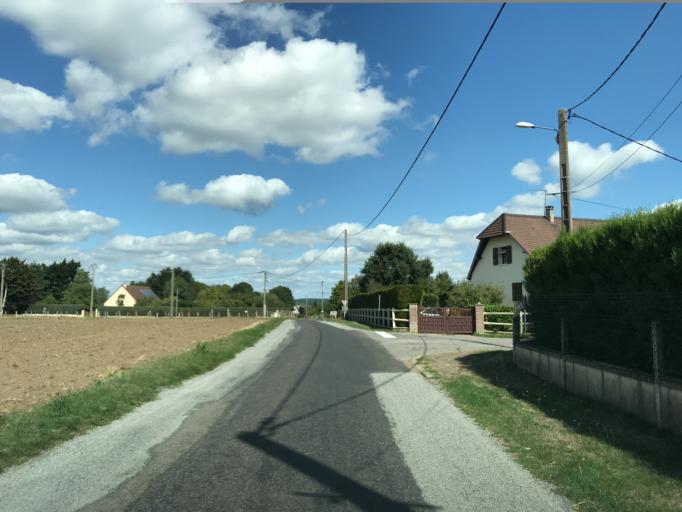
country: FR
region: Haute-Normandie
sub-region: Departement de l'Eure
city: La Chapelle-Reanville
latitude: 49.1336
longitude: 1.3948
